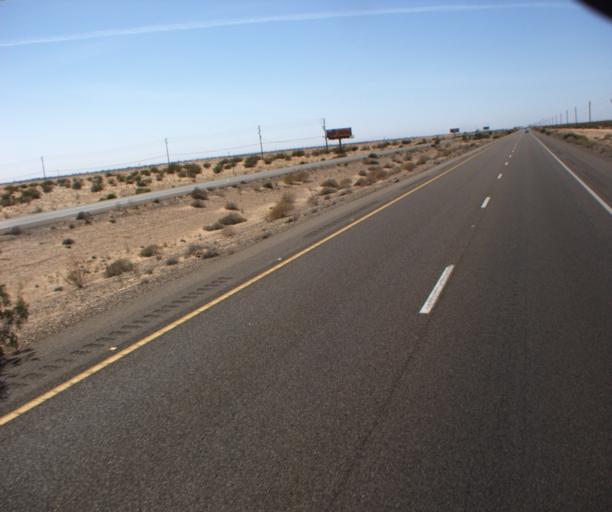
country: MX
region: Sonora
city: San Luis Rio Colorado
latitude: 32.4947
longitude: -114.6814
